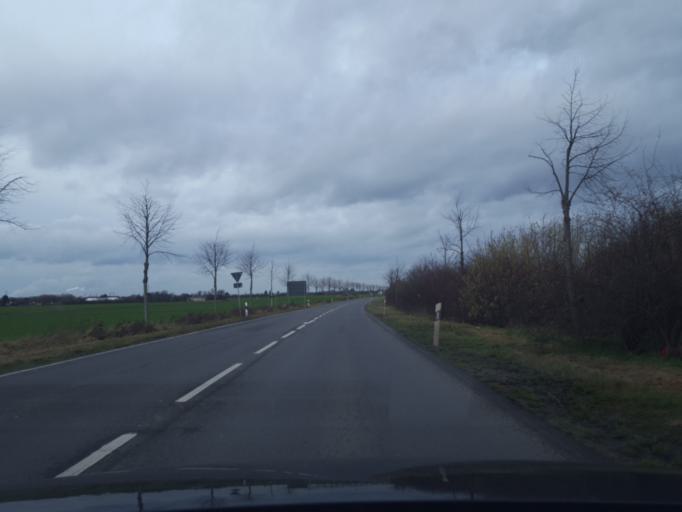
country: DE
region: North Rhine-Westphalia
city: Niederkassel
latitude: 50.8161
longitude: 7.0492
